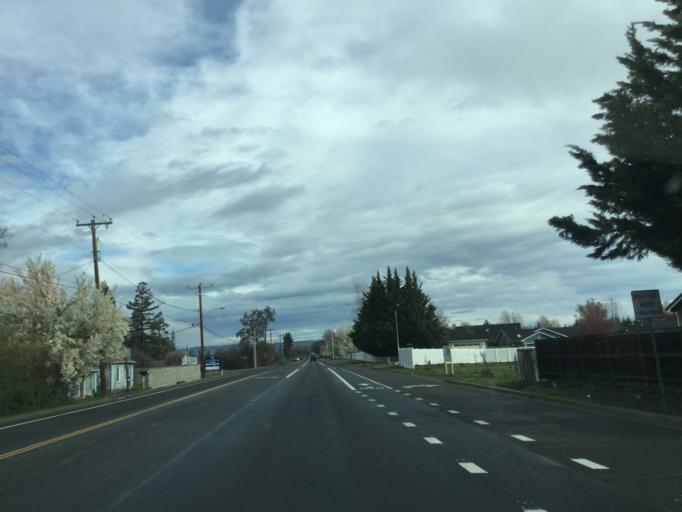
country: US
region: Oregon
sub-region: Jackson County
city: Central Point
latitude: 42.3815
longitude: -122.8929
